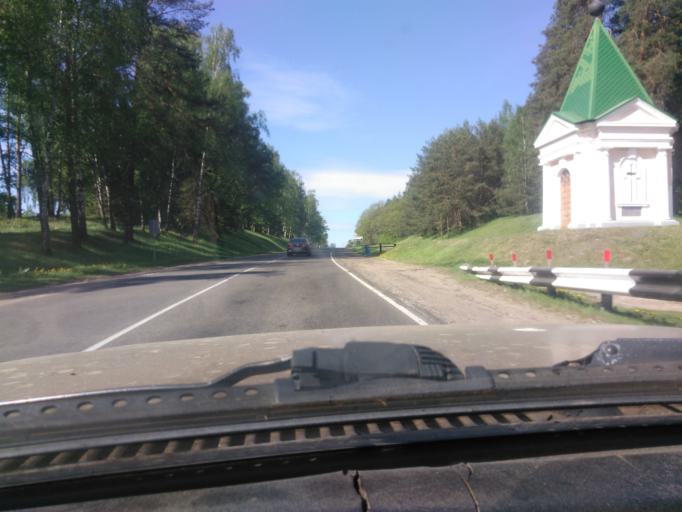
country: BY
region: Mogilev
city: Buynichy
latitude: 53.8127
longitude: 30.2311
